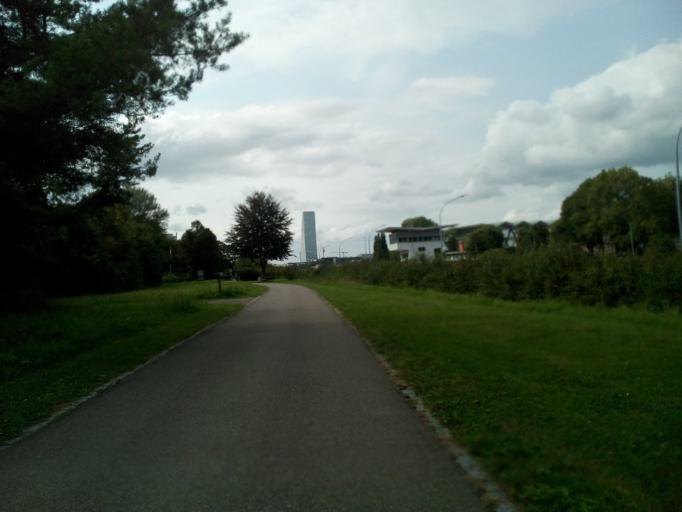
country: CH
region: Basel-Landschaft
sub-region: Bezirk Arlesheim
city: Birsfelden
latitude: 47.5587
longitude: 7.6302
